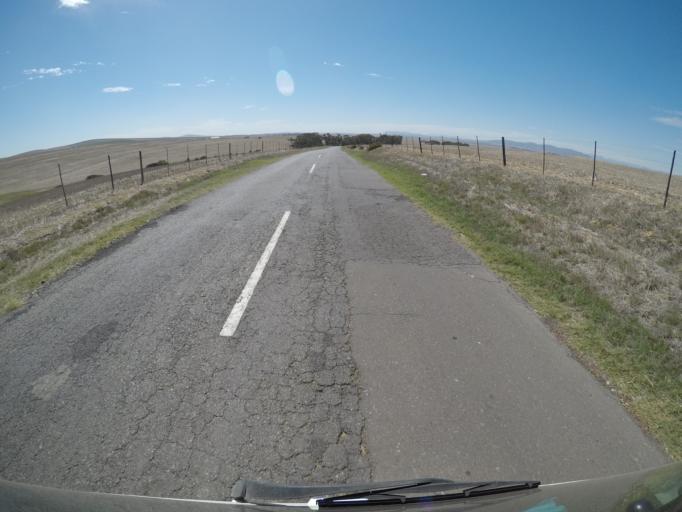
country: ZA
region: Western Cape
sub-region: City of Cape Town
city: Atlantis
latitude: -33.7037
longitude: 18.5867
